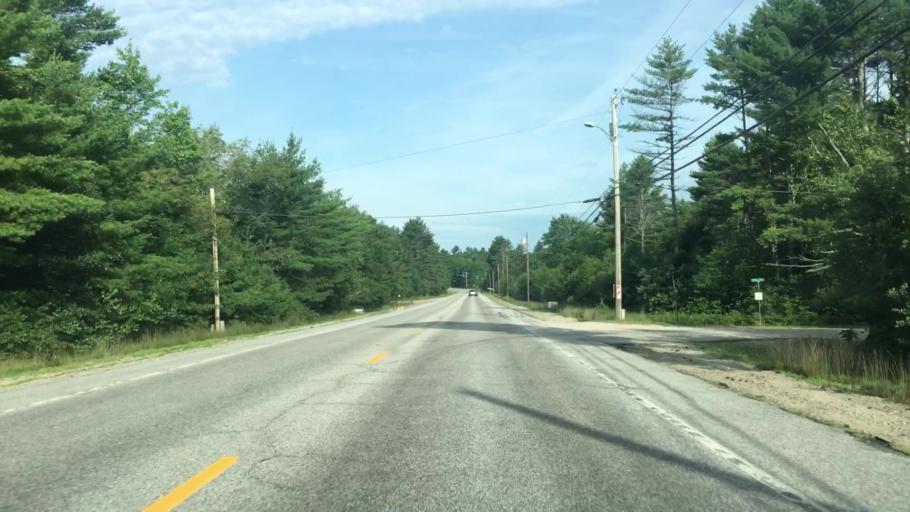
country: US
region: Maine
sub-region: Cumberland County
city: Steep Falls
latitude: 43.7357
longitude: -70.6240
